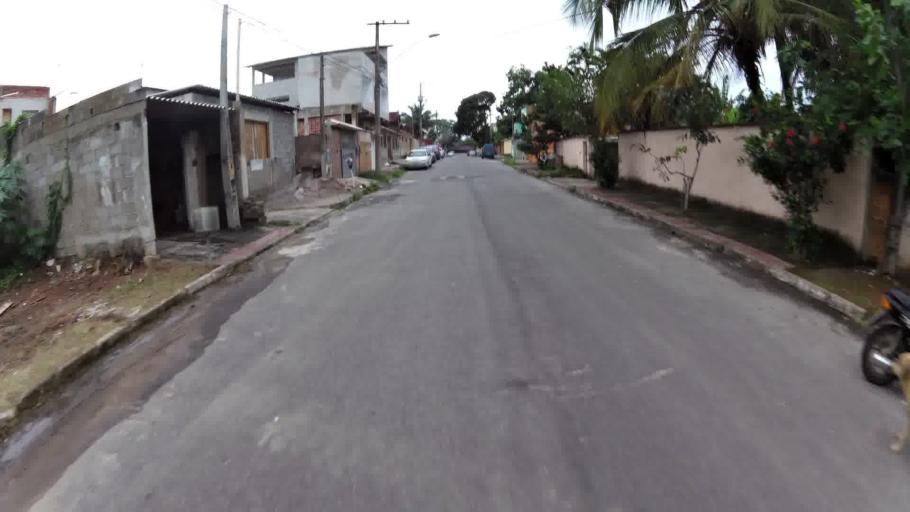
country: BR
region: Espirito Santo
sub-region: Guarapari
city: Guarapari
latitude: -20.6493
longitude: -40.4898
